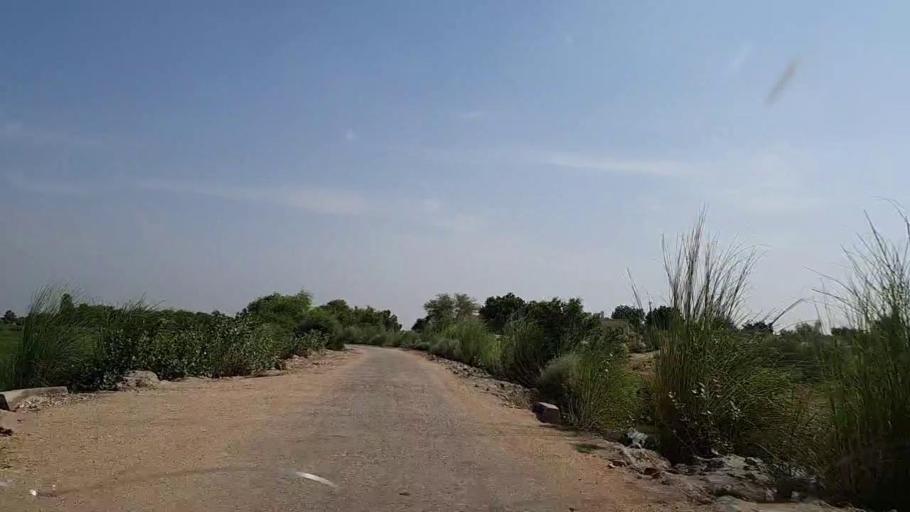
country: PK
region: Sindh
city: Khanpur
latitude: 27.7129
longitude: 69.3621
